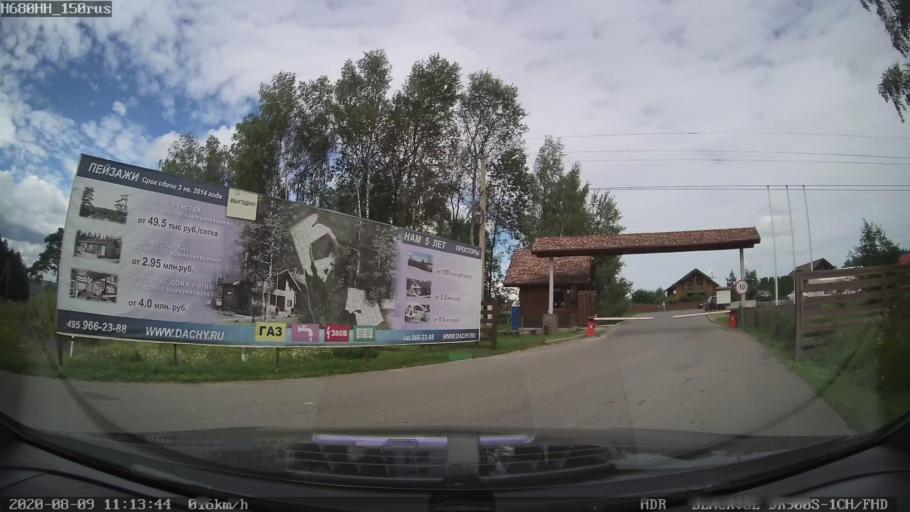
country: RU
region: Tula
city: Zaokskiy
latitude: 54.7316
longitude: 37.3326
